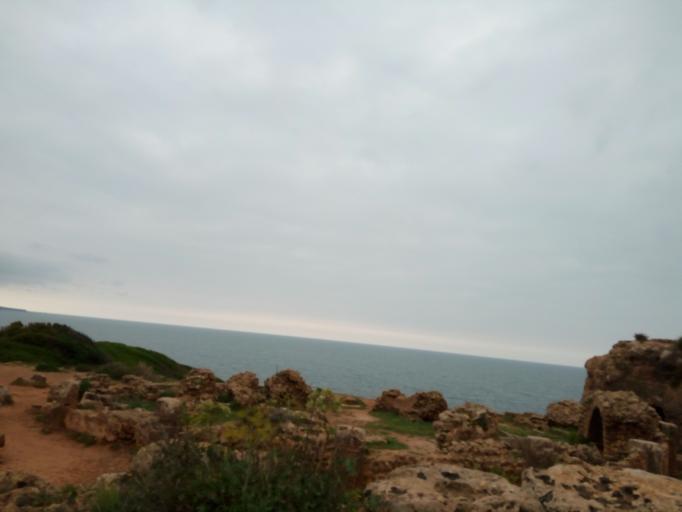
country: DZ
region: Tipaza
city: Tipasa
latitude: 36.5953
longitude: 2.4398
